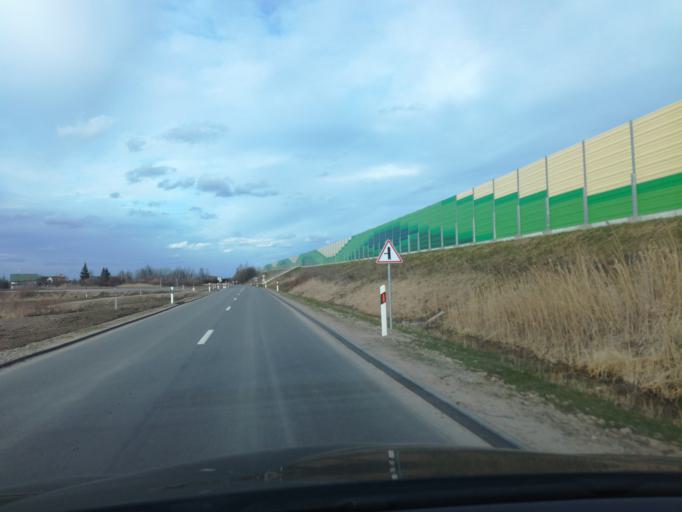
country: LT
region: Marijampoles apskritis
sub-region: Marijampole Municipality
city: Marijampole
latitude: 54.6102
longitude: 23.4108
